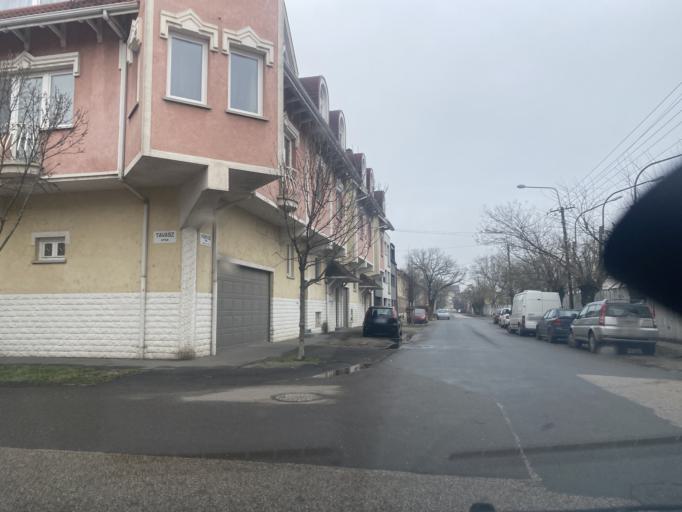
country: HU
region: Csongrad
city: Szeged
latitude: 46.2627
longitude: 20.1409
